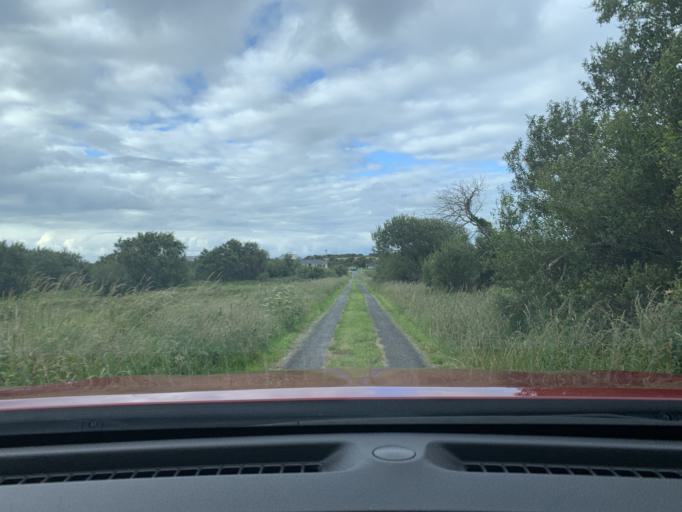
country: IE
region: Connaught
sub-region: County Leitrim
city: Kinlough
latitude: 54.4611
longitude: -8.3545
